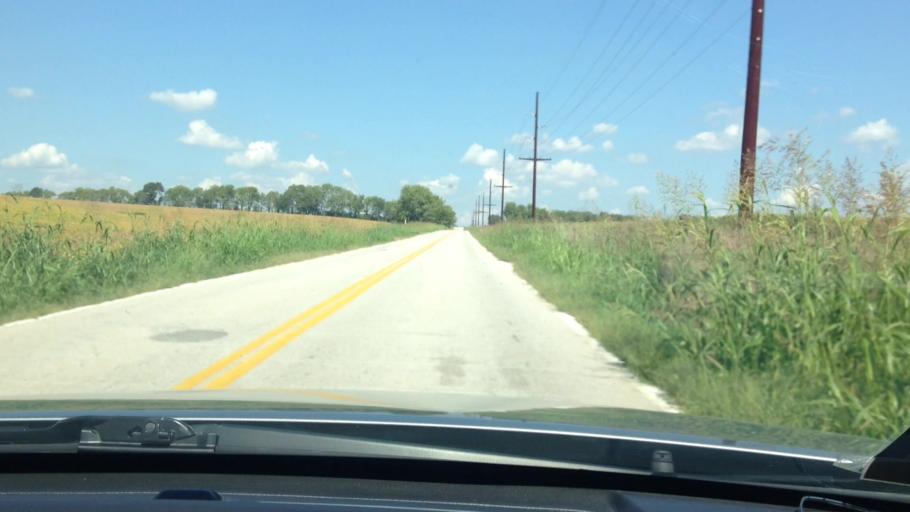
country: US
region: Missouri
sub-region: Platte County
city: Platte City
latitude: 39.3423
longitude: -94.7330
